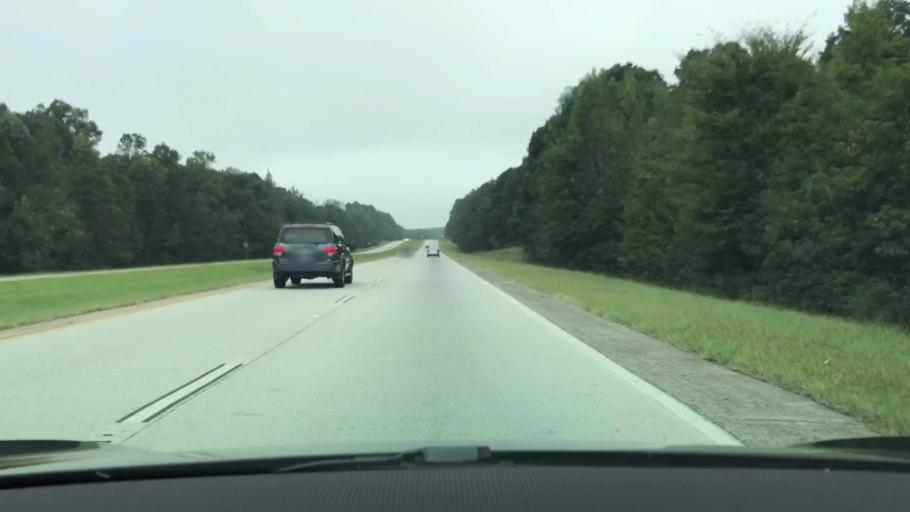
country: US
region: Georgia
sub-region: Barrow County
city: Statham
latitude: 33.9444
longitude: -83.5708
